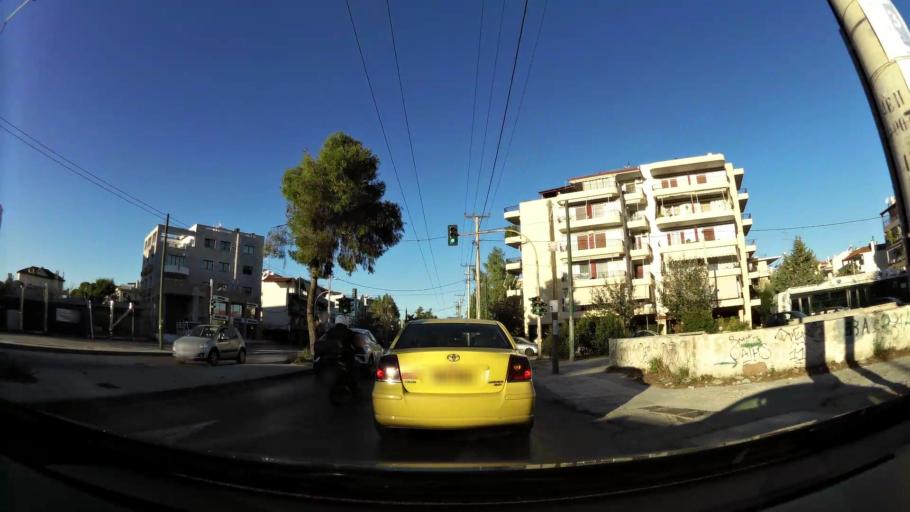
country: GR
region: Attica
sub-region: Nomarchia Athinas
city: Khalandrion
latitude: 38.0205
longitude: 23.8140
